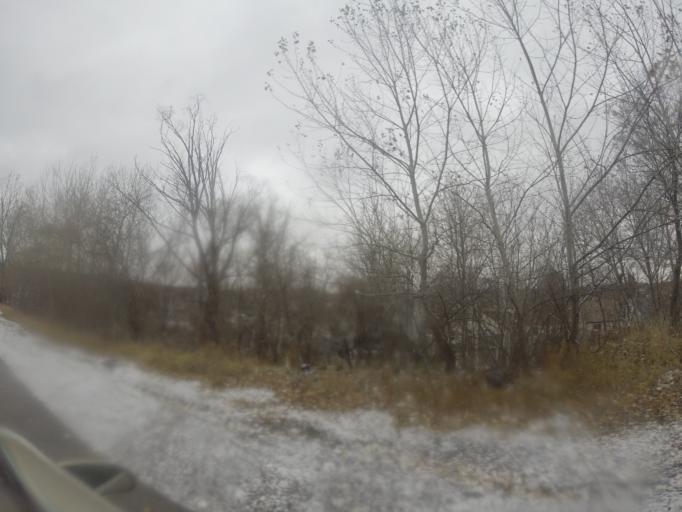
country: CA
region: Ontario
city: Greater Sudbury
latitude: 46.4957
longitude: -81.0054
